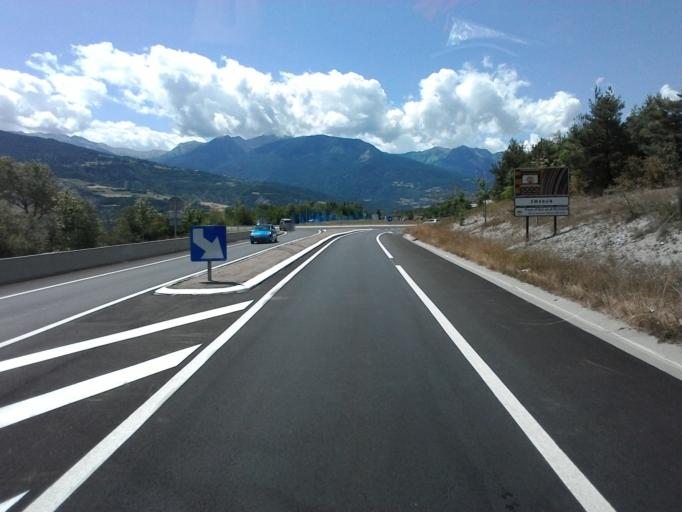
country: FR
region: Provence-Alpes-Cote d'Azur
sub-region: Departement des Hautes-Alpes
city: Embrun
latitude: 44.5876
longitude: 6.5137
